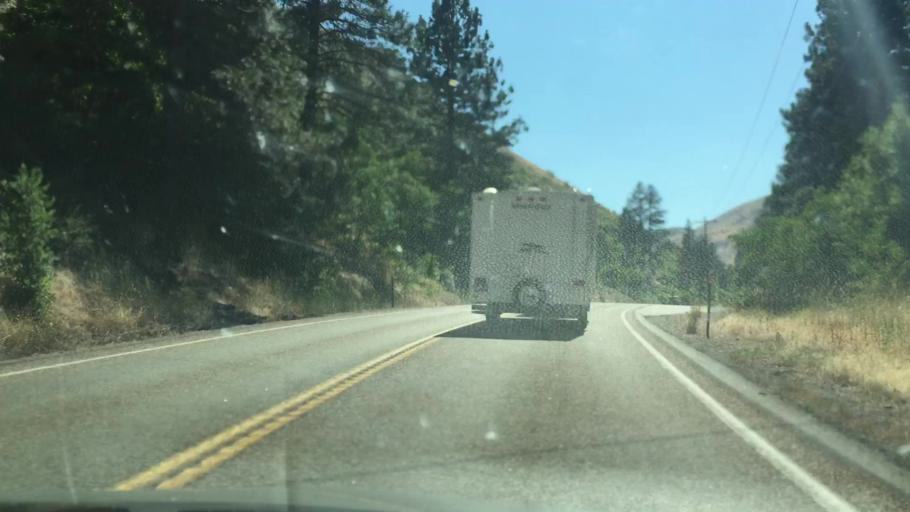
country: US
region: Idaho
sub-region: Boise County
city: Idaho City
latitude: 44.0267
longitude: -116.1369
